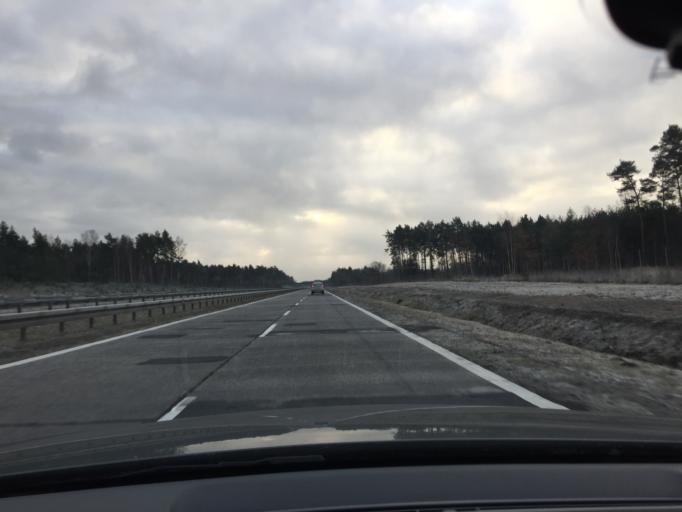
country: PL
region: Lubusz
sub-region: Powiat zarski
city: Lipinki Luzyckie
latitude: 51.5821
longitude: 15.0238
